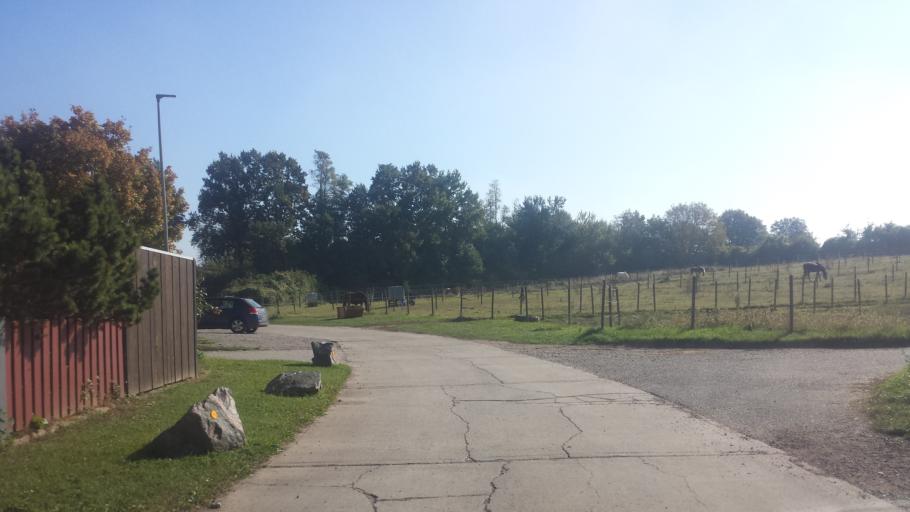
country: DE
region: Rheinland-Pfalz
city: Insheim
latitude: 49.1541
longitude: 8.1491
